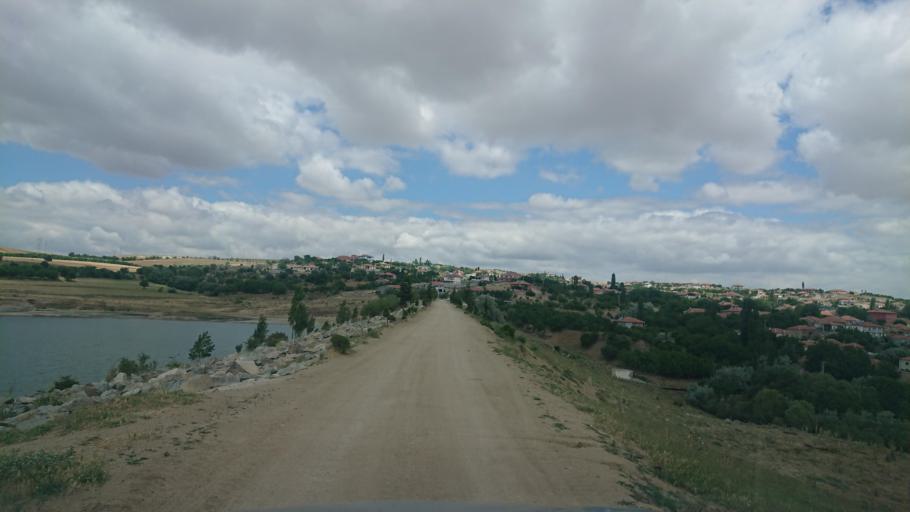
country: TR
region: Aksaray
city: Agacoren
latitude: 38.8646
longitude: 33.9514
